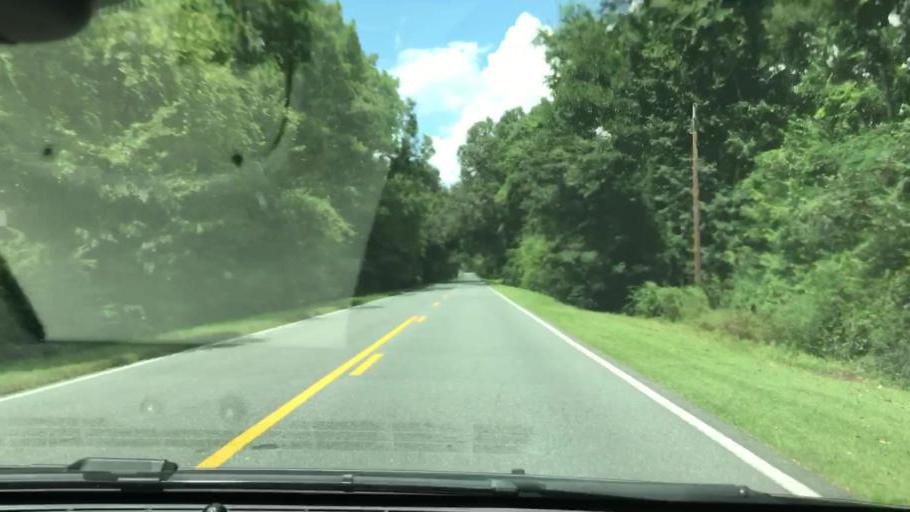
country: US
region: Florida
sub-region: Jackson County
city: Malone
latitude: 30.9447
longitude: -85.1183
